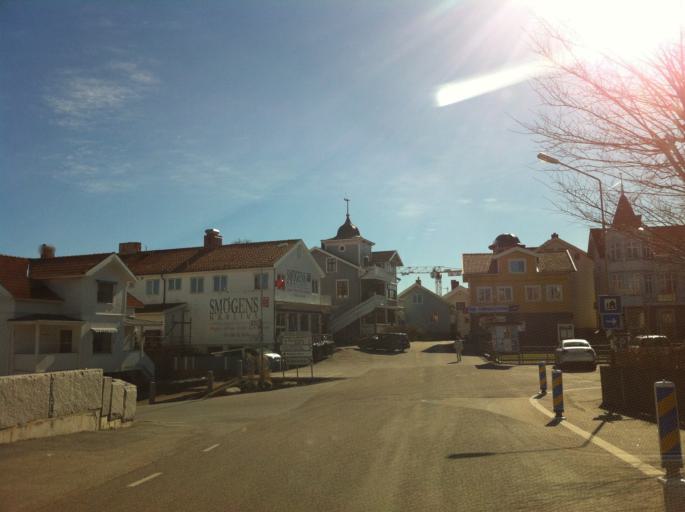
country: SE
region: Vaestra Goetaland
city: Smoegen
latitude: 58.3549
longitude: 11.2253
